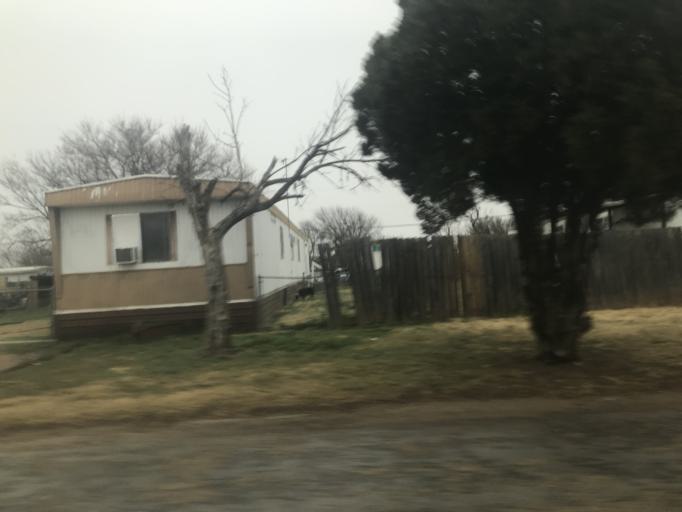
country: US
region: Texas
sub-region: Taylor County
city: Tye
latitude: 32.4444
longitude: -99.8116
